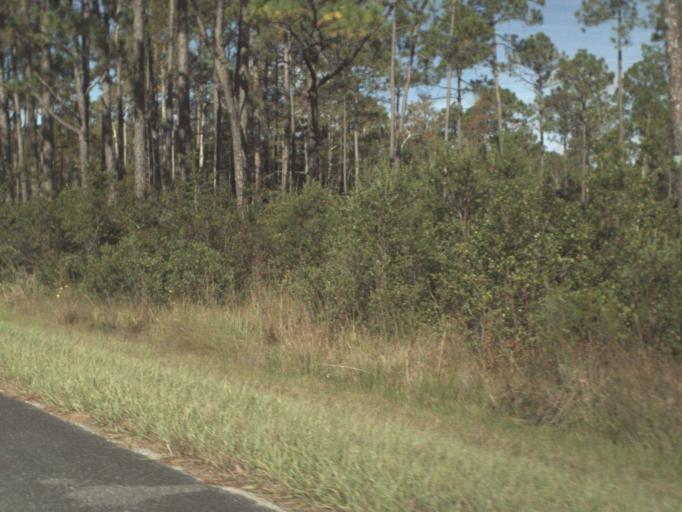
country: US
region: Florida
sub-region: Franklin County
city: Eastpoint
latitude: 29.8287
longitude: -84.8650
